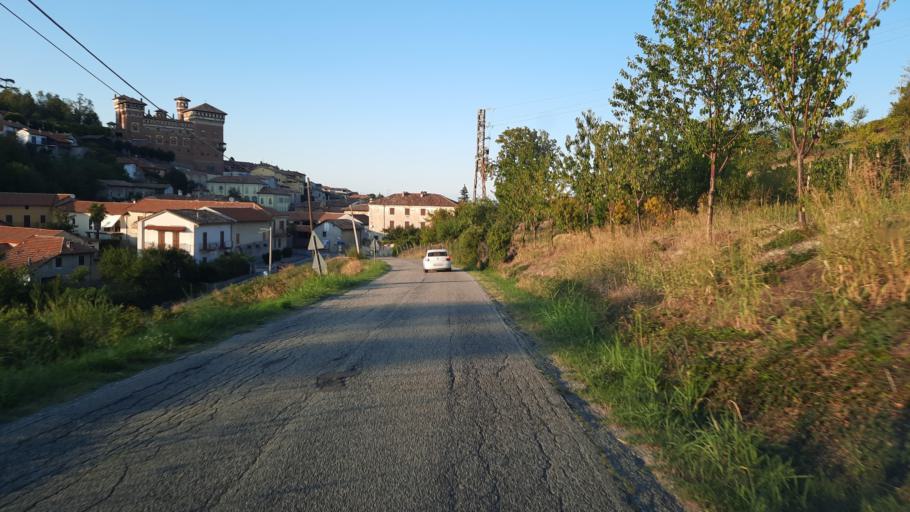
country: IT
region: Piedmont
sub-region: Provincia di Alessandria
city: Cereseto
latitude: 45.0833
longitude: 8.3161
